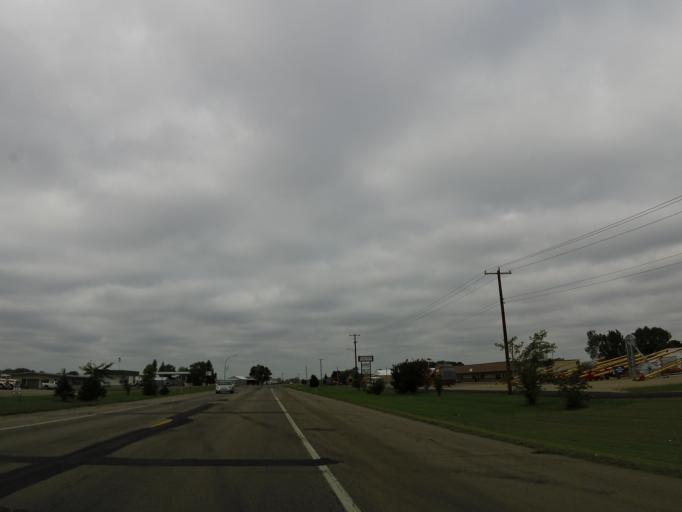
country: US
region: Minnesota
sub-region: Renville County
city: Olivia
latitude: 44.7780
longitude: -95.0224
